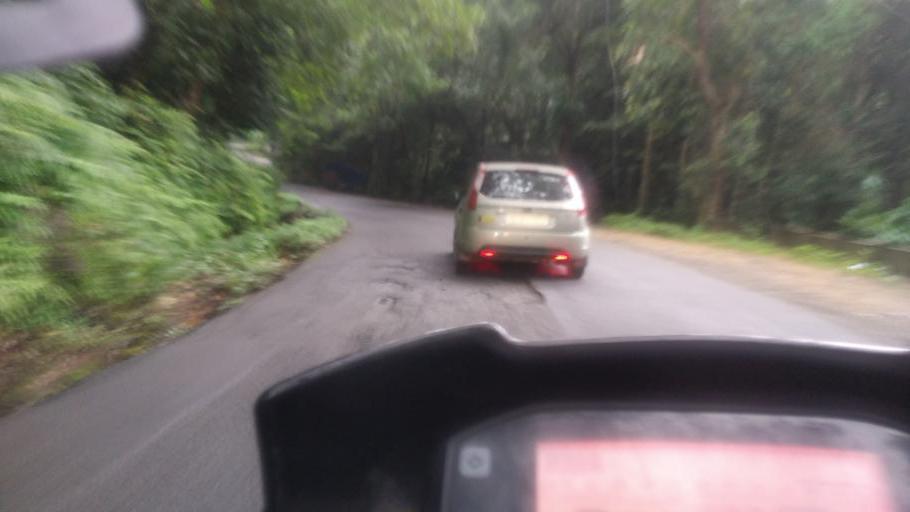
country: IN
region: Kerala
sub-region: Idukki
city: Kuttampuzha
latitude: 10.0649
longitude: 76.7966
